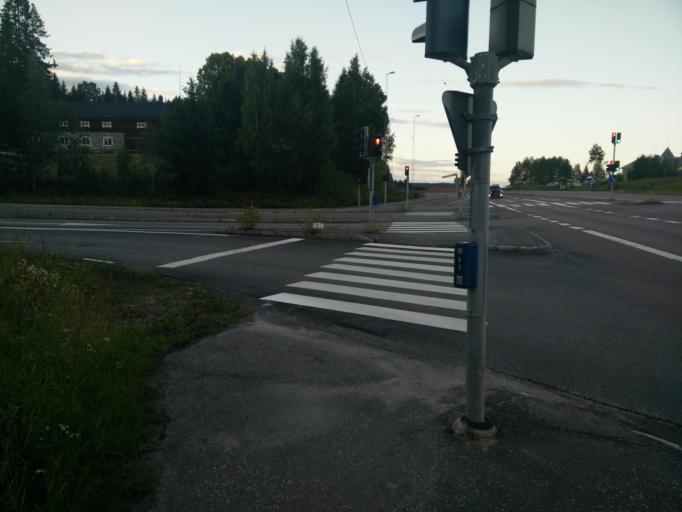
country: SE
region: Vaesternorrland
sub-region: Sundsvalls Kommun
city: Njurundabommen
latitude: 62.2728
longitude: 17.3746
